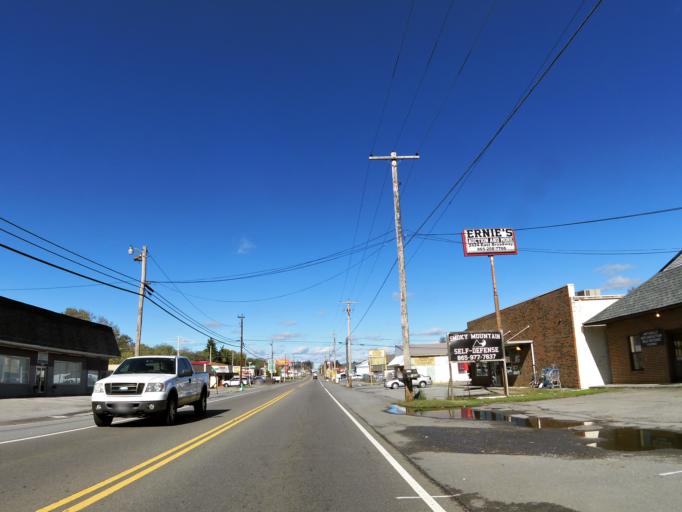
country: US
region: Tennessee
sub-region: Blount County
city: Eagleton Village
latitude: 35.7875
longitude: -83.9469
